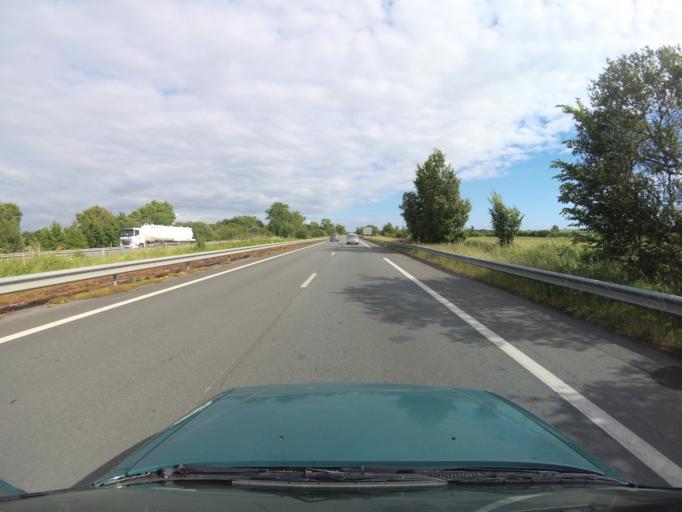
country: FR
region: Poitou-Charentes
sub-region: Departement de la Charente-Maritime
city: Chatelaillon-Plage
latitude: 46.0727
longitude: -1.0704
